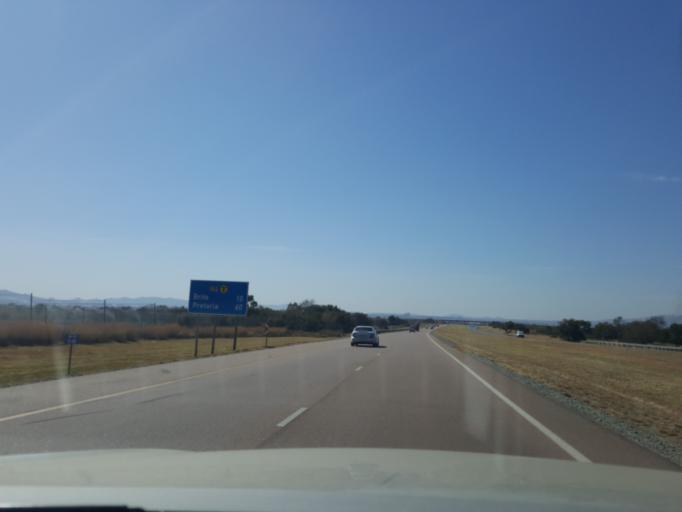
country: ZA
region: North-West
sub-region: Bojanala Platinum District Municipality
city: Brits
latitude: -25.6902
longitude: 27.7465
